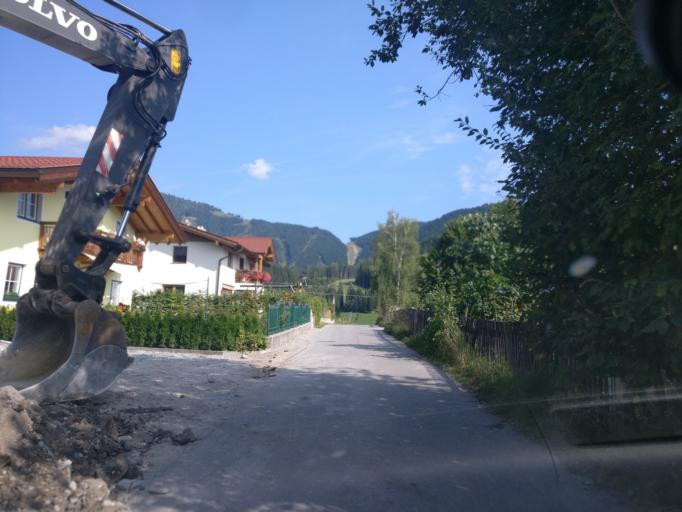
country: AT
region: Salzburg
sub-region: Politischer Bezirk Sankt Johann im Pongau
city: Werfenweng
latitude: 47.4621
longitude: 13.2462
